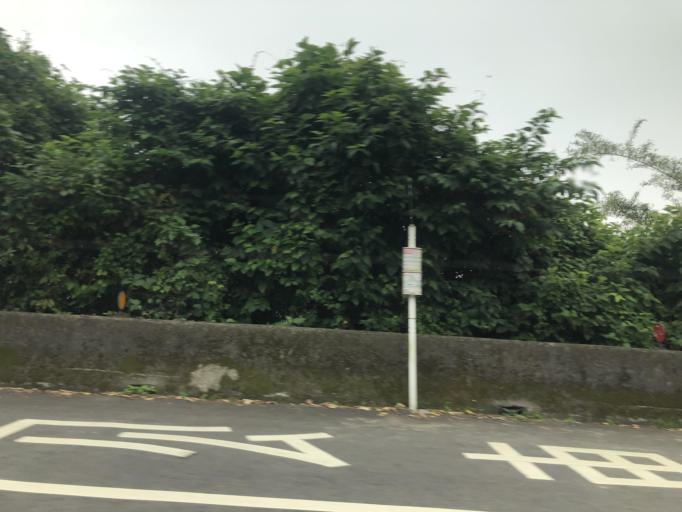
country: TW
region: Taiwan
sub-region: Keelung
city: Keelung
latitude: 25.1915
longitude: 121.6799
